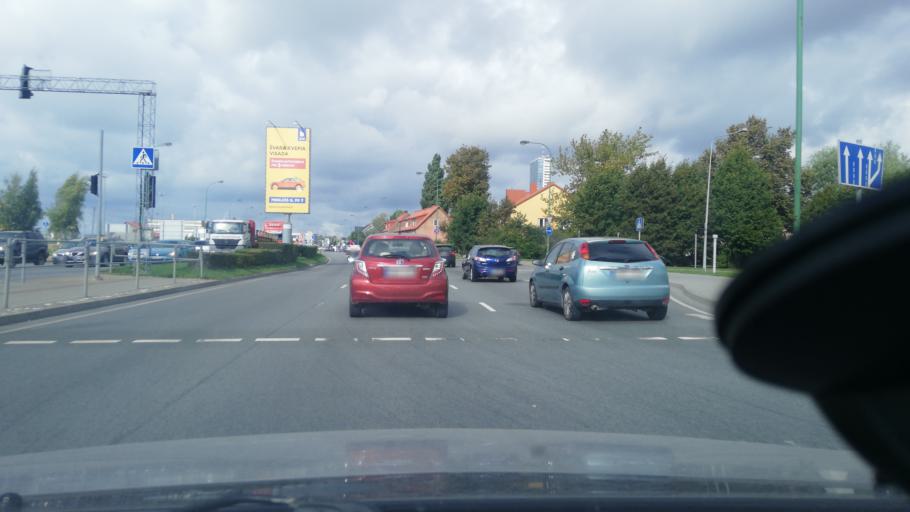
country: LT
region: Klaipedos apskritis
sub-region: Klaipeda
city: Klaipeda
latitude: 55.6840
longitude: 21.1493
